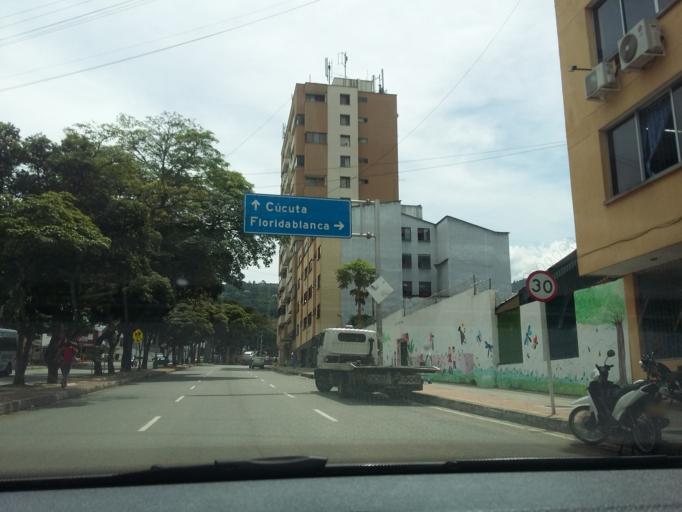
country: CO
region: Santander
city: Bucaramanga
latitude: 7.1299
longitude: -73.1142
